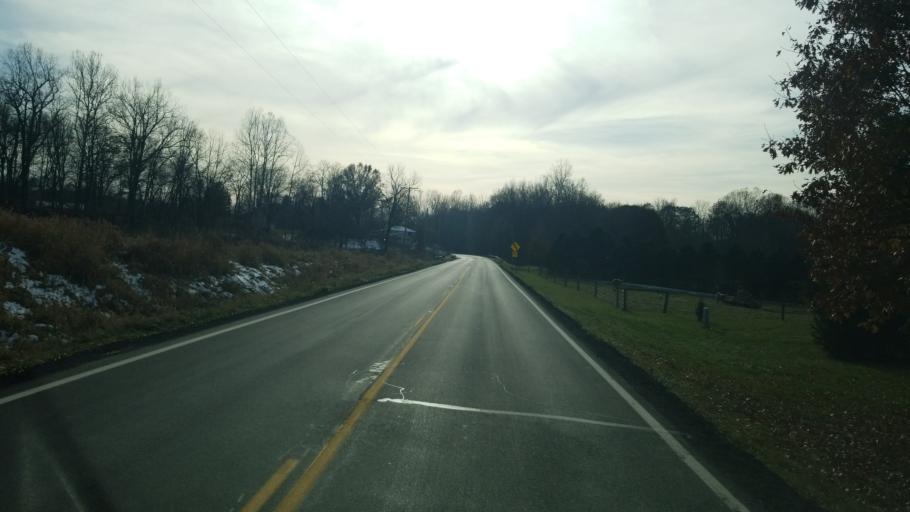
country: US
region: Ohio
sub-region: Ashland County
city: Ashland
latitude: 40.9619
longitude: -82.2550
